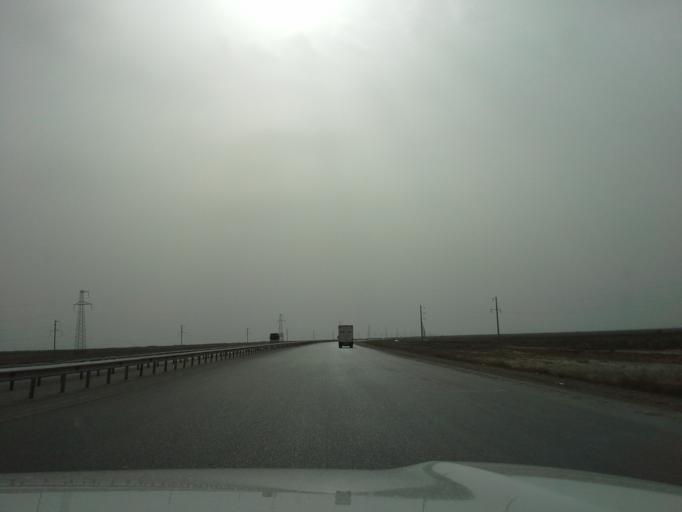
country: IR
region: Razavi Khorasan
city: Dargaz
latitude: 37.5470
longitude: 59.3887
